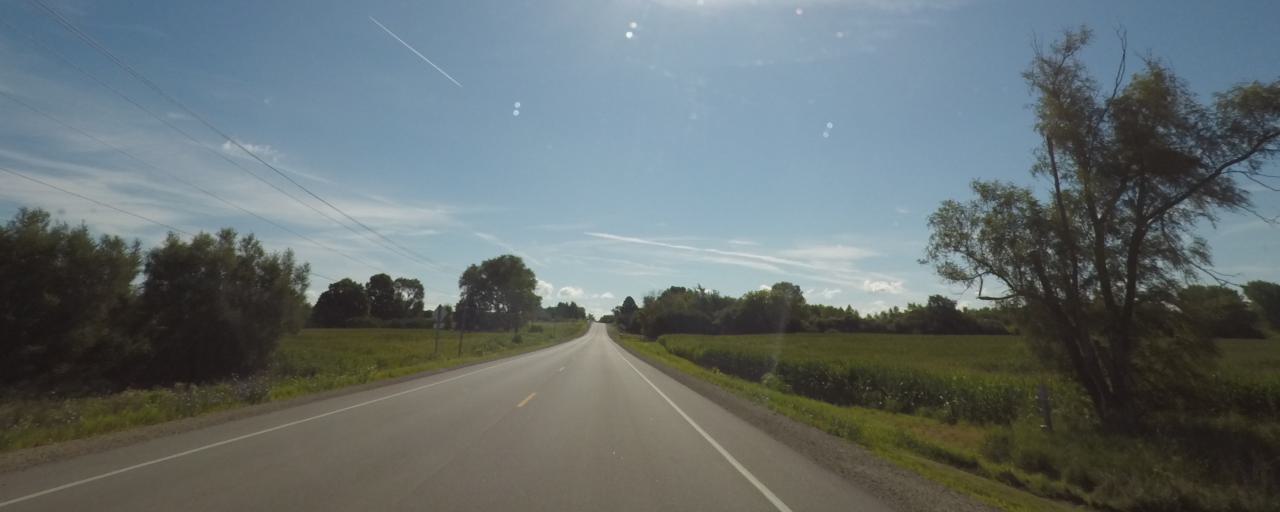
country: US
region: Wisconsin
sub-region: Jefferson County
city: Johnson Creek
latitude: 43.0758
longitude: -88.7343
